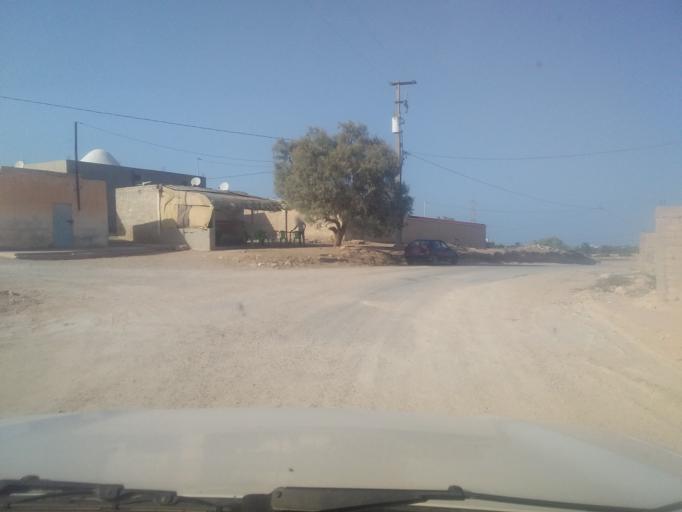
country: TN
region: Qabis
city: Matmata
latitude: 33.5836
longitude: 10.2657
